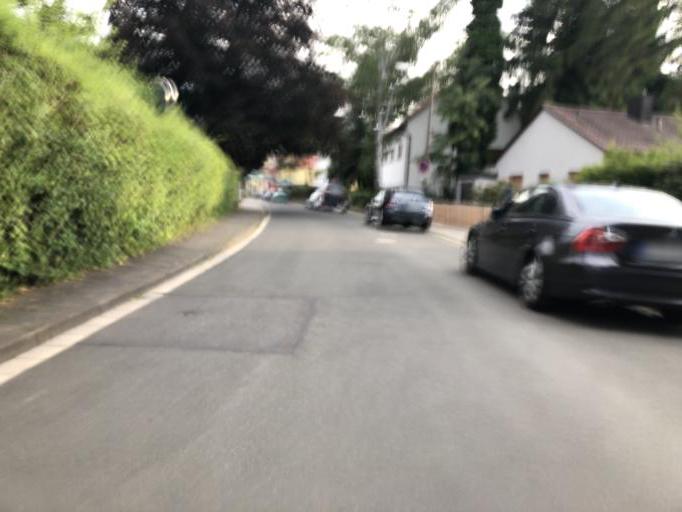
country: DE
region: Bavaria
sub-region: Regierungsbezirk Mittelfranken
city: Erlangen
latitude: 49.5909
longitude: 10.9942
